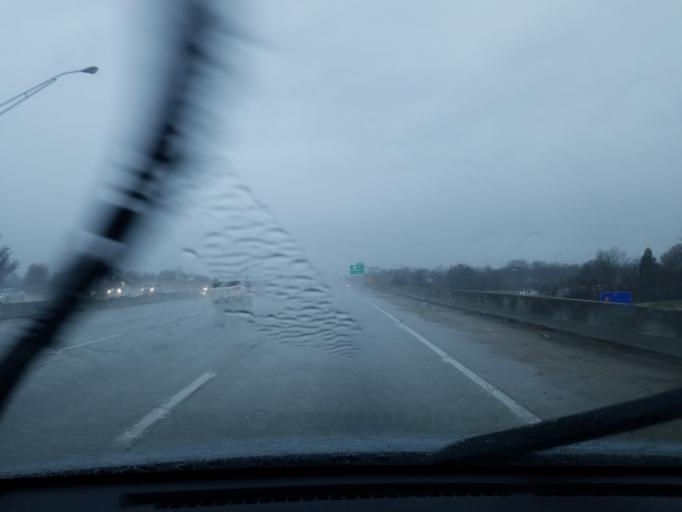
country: US
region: Kentucky
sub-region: Jefferson County
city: Buechel
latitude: 38.2221
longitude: -85.6500
